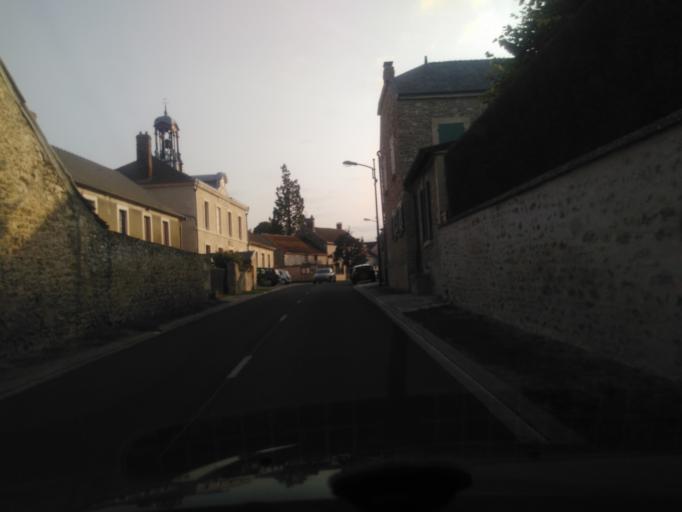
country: FR
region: Champagne-Ardenne
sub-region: Departement de la Marne
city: Fismes
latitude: 49.2352
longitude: 3.6948
